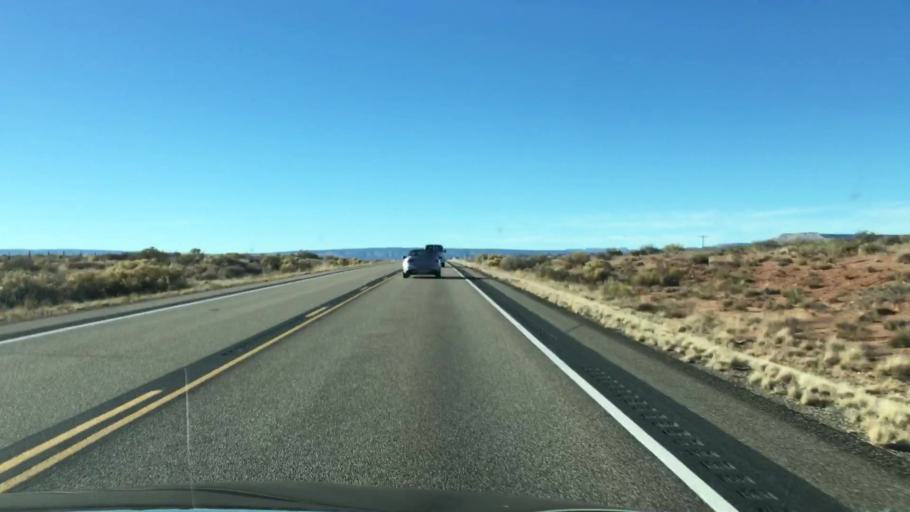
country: US
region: Arizona
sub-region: Coconino County
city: Page
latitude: 37.0953
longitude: -111.7602
